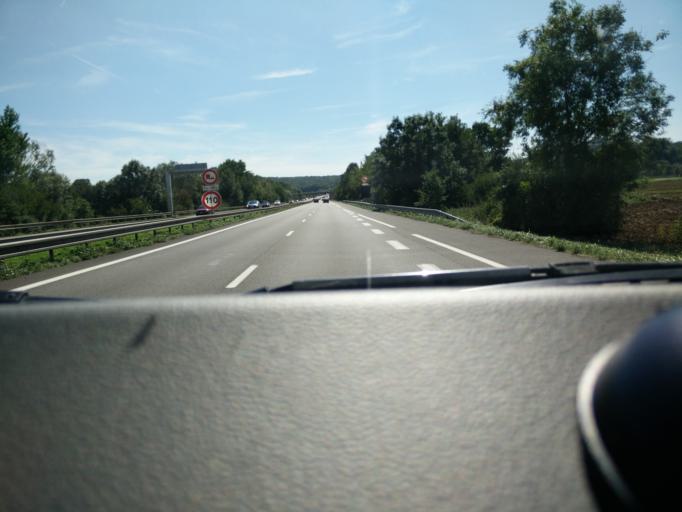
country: FR
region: Lorraine
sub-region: Departement de la Moselle
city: Entrange
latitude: 49.4016
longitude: 6.1115
